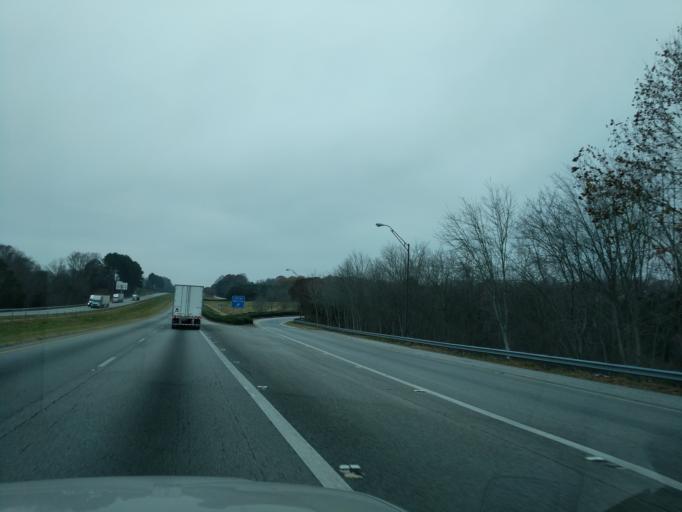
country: US
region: Georgia
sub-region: Franklin County
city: Gumlog
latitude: 34.4716
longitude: -83.0655
